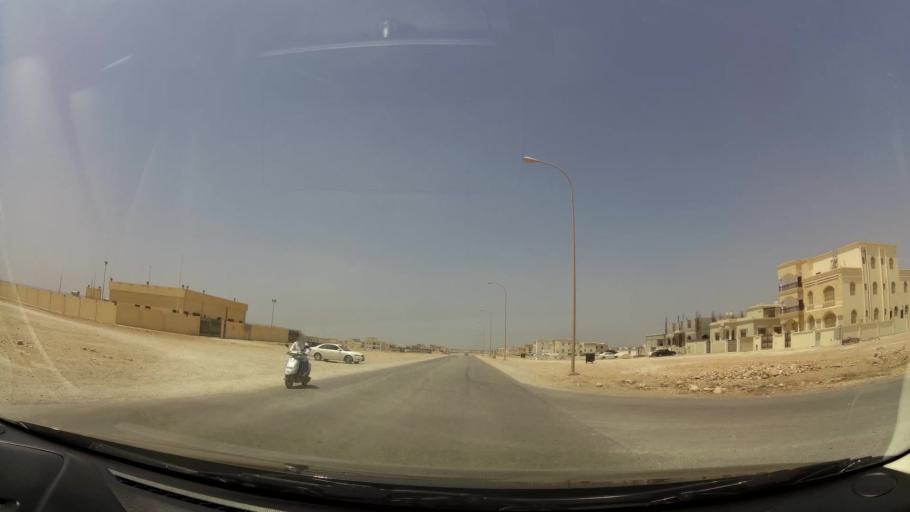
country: OM
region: Zufar
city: Salalah
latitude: 17.0768
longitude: 54.2053
